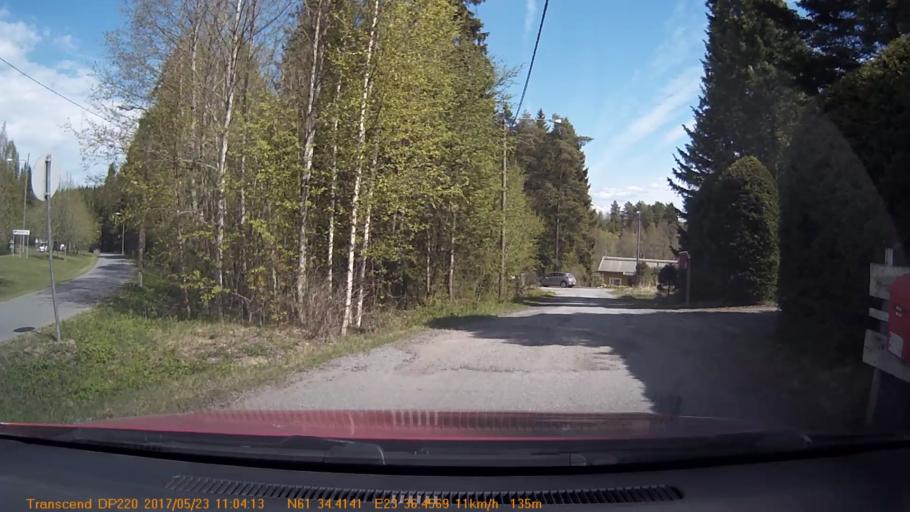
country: FI
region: Pirkanmaa
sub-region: Tampere
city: Yloejaervi
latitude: 61.5736
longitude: 23.6077
